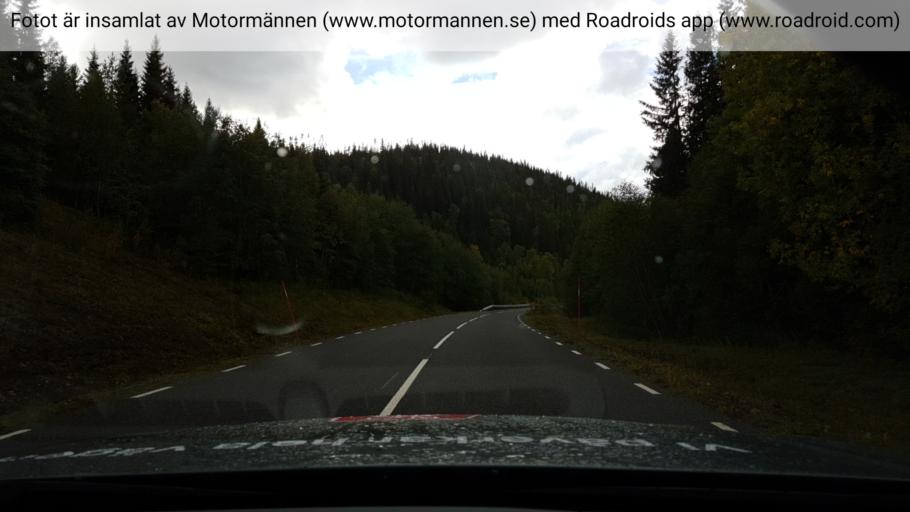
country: SE
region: Jaemtland
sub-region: Are Kommun
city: Are
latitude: 63.6058
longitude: 13.1844
